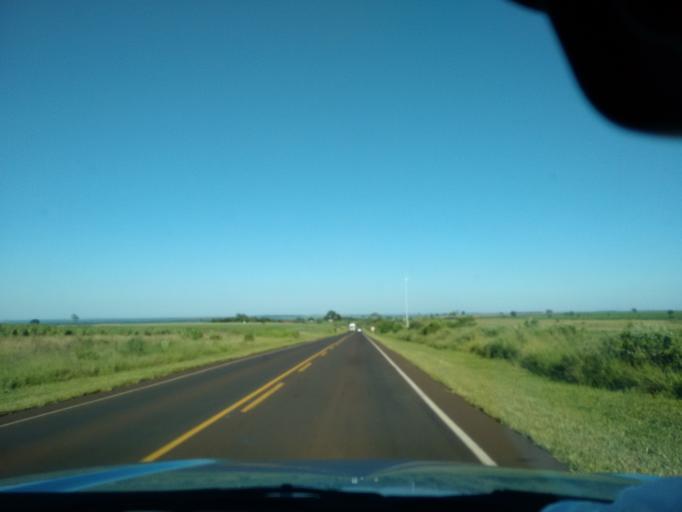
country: BR
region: Mato Grosso do Sul
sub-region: Caarapo
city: Caarapo
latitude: -22.8180
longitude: -54.7026
